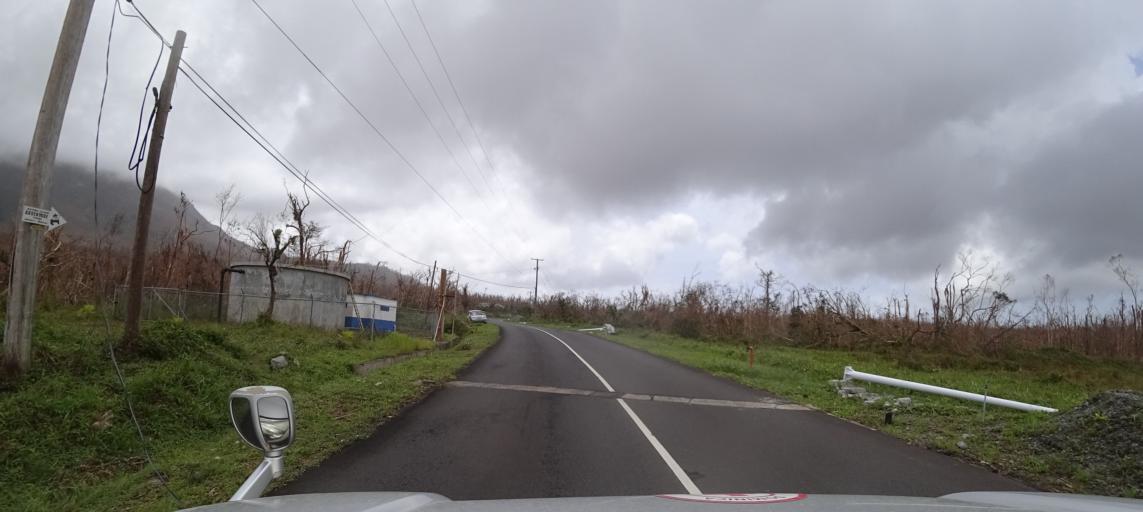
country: DM
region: Saint Paul
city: Pont Casse
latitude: 15.3946
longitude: -61.3458
